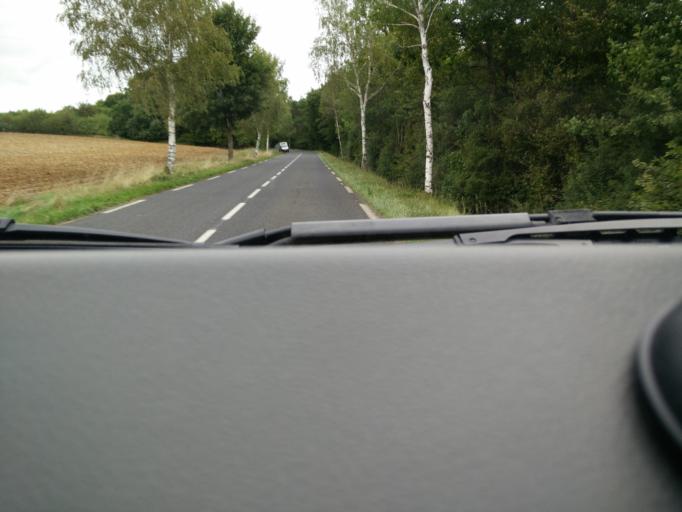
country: FR
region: Lorraine
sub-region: Departement de Meurthe-et-Moselle
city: Montauville
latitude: 48.9420
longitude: 5.8871
